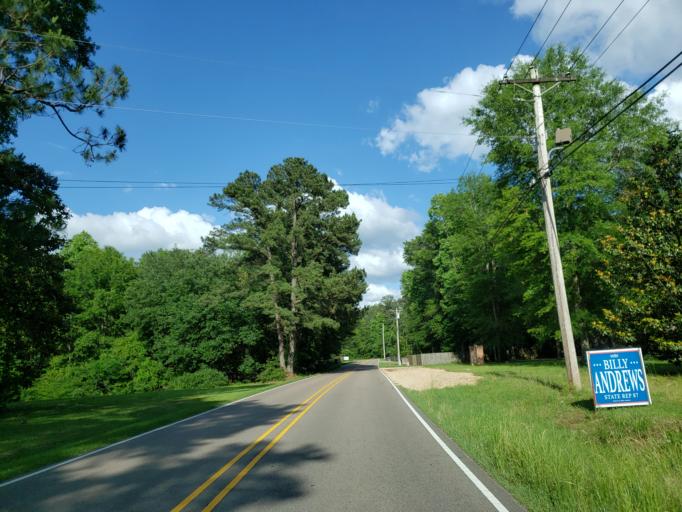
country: US
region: Mississippi
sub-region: Lamar County
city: West Hattiesburg
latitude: 31.2721
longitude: -89.4070
